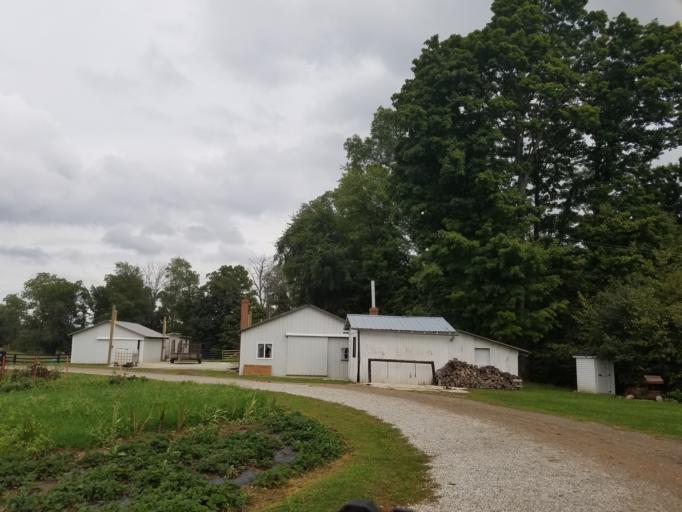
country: US
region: Ohio
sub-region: Knox County
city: Fredericktown
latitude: 40.5448
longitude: -82.6609
